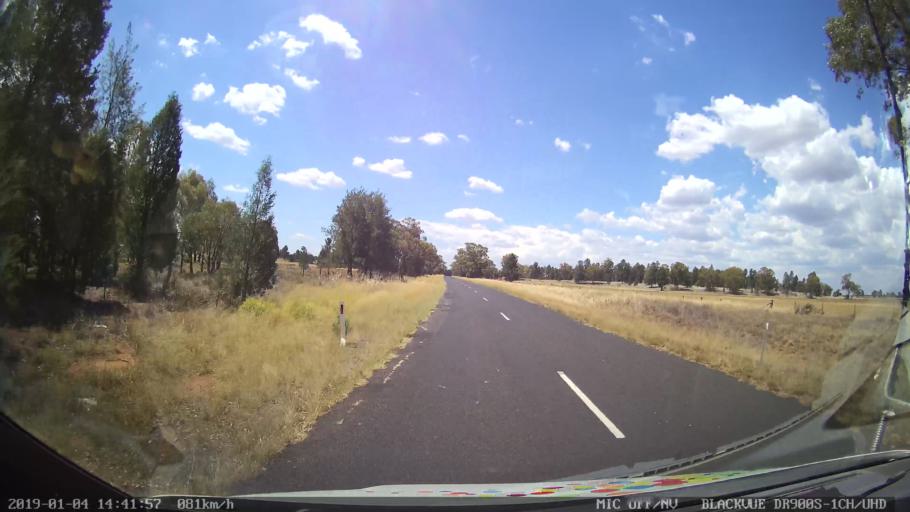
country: AU
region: New South Wales
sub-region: Dubbo Municipality
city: Dubbo
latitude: -32.1338
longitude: 148.6393
